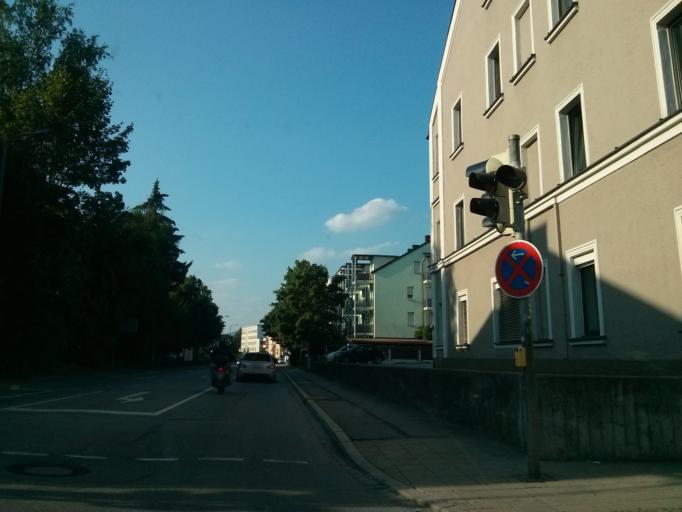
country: DE
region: Bavaria
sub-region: Lower Bavaria
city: Deggendorf
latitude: 48.8340
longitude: 12.9584
